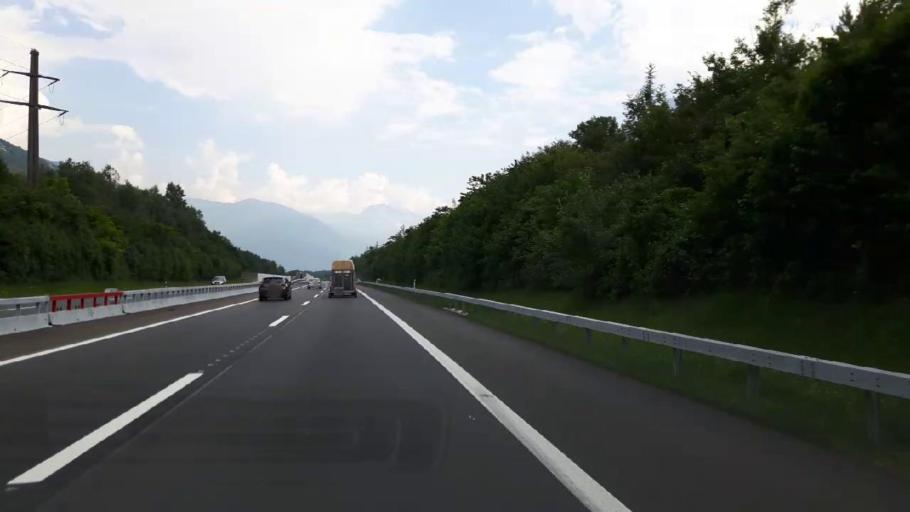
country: CH
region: Ticino
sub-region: Riviera District
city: Lodrino
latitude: 46.3058
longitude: 8.9840
